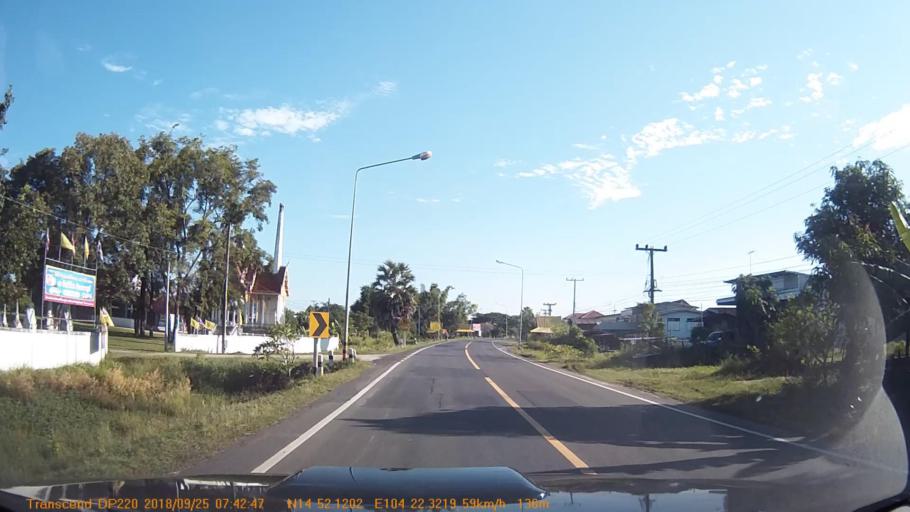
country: TH
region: Sisaket
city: Phayu
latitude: 14.8689
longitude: 104.3721
